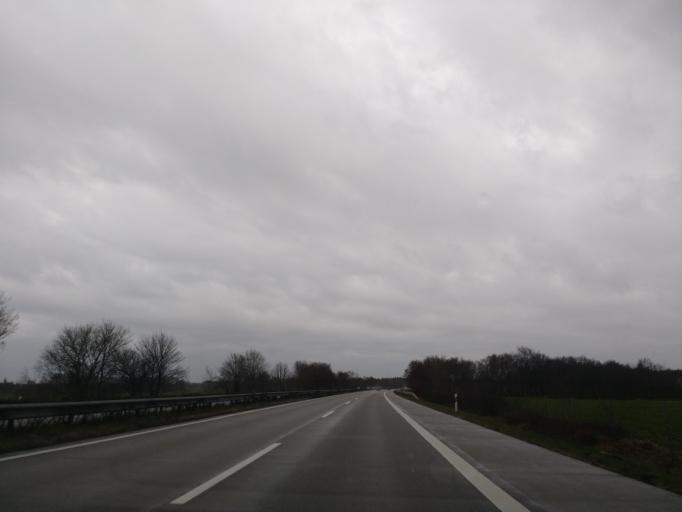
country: DE
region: Lower Saxony
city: Midlum
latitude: 53.7679
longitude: 8.6980
